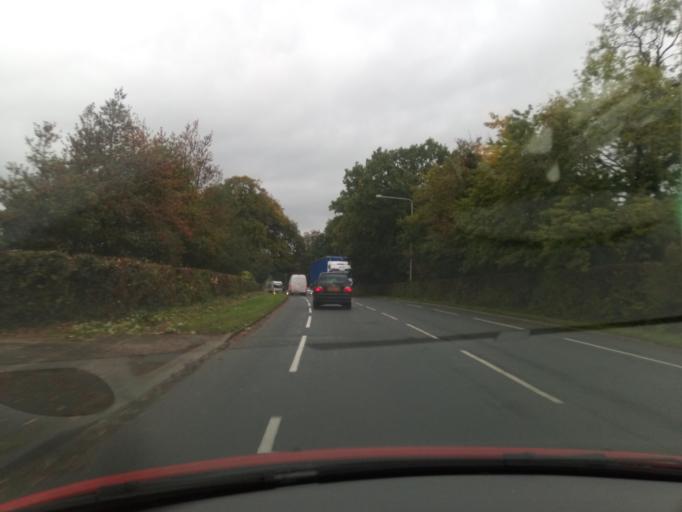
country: GB
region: England
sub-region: Lancashire
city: Catterall
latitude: 53.8404
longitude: -2.7402
